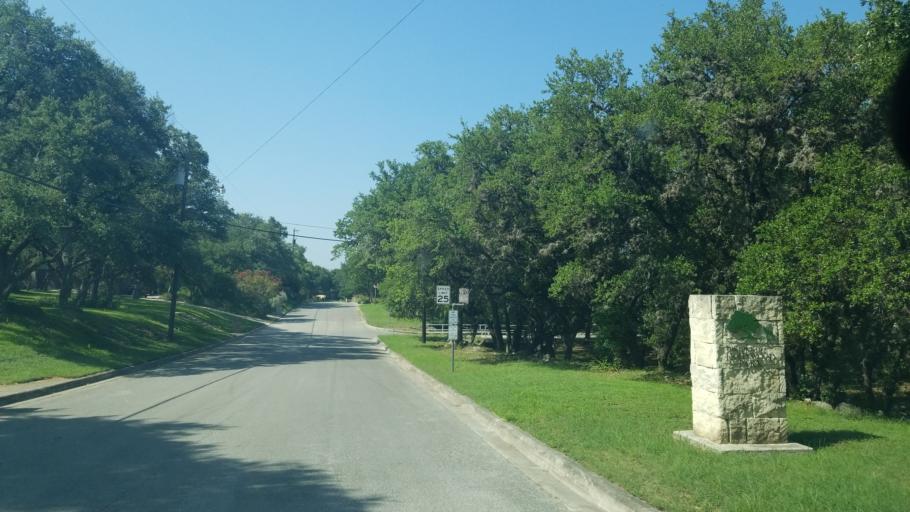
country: US
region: Texas
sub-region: Bexar County
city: Hollywood Park
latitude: 29.6077
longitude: -98.4757
